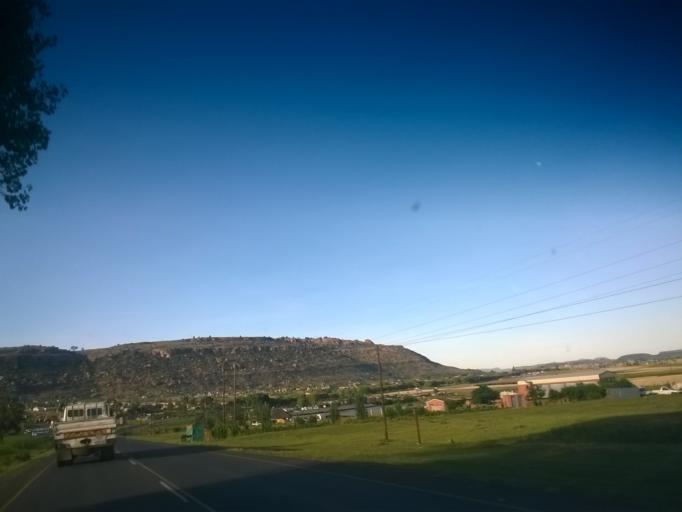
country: LS
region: Maseru
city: Maseru
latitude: -29.2650
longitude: 27.6001
